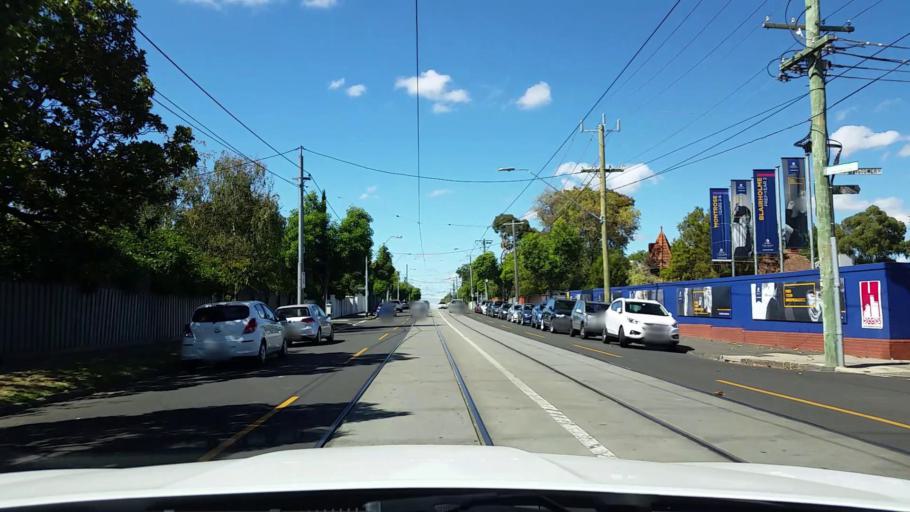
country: AU
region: Victoria
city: Toorak
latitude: -37.8509
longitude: 145.0248
